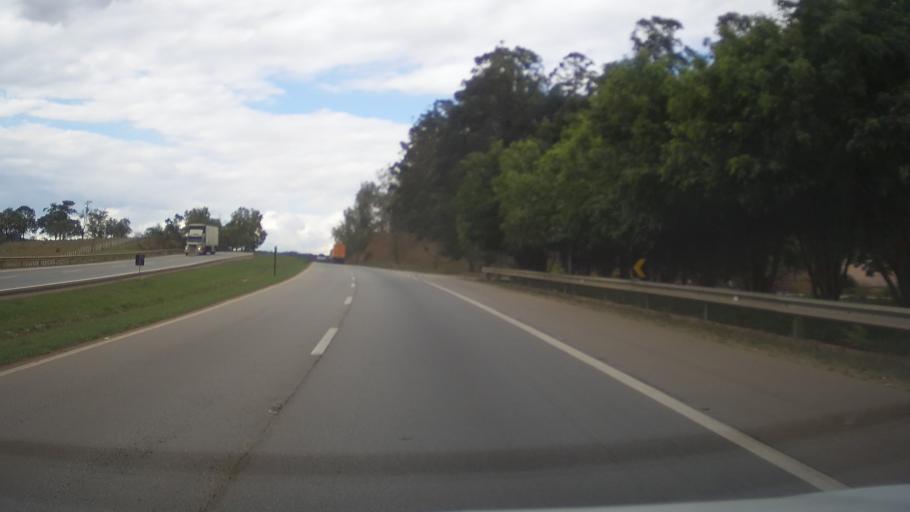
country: BR
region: Minas Gerais
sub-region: Itauna
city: Itauna
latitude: -20.2941
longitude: -44.4370
